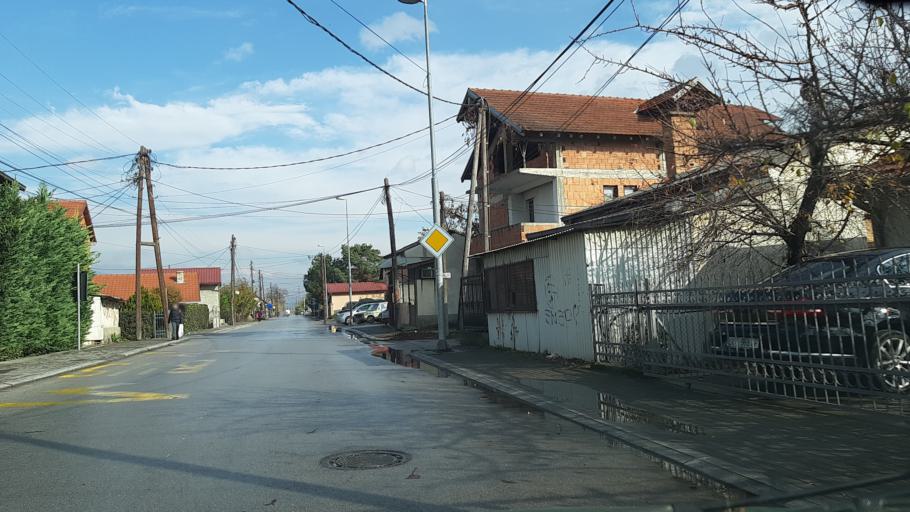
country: MK
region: Kisela Voda
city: Kisela Voda
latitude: 41.9794
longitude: 21.4871
